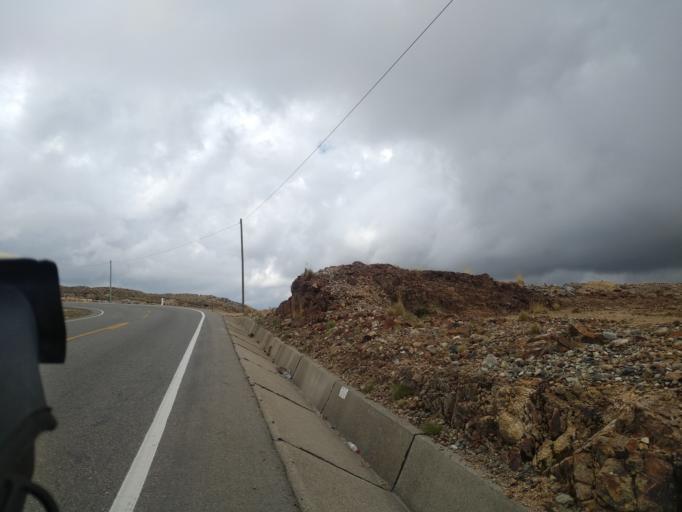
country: PE
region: La Libertad
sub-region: Provincia de Santiago de Chuco
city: Quiruvilca
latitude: -7.9546
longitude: -78.1940
